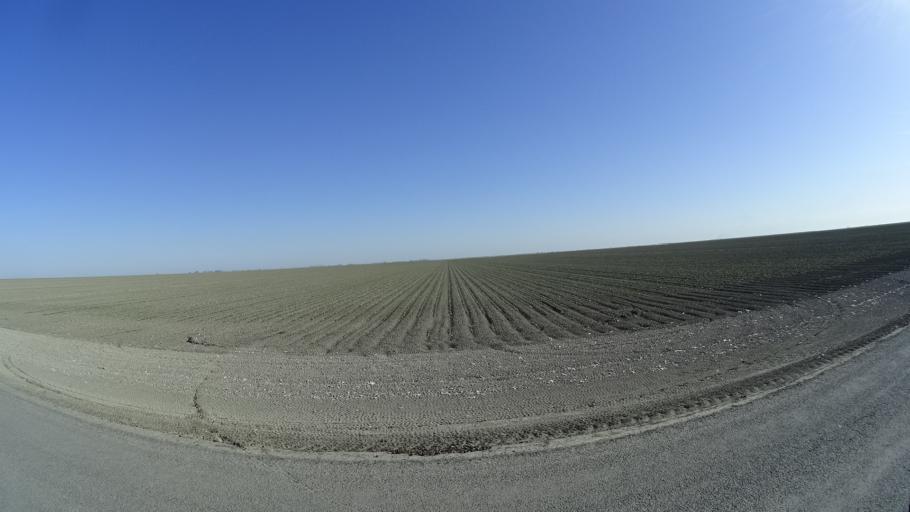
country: US
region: California
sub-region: Kings County
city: Stratford
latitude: 36.0797
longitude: -119.7579
